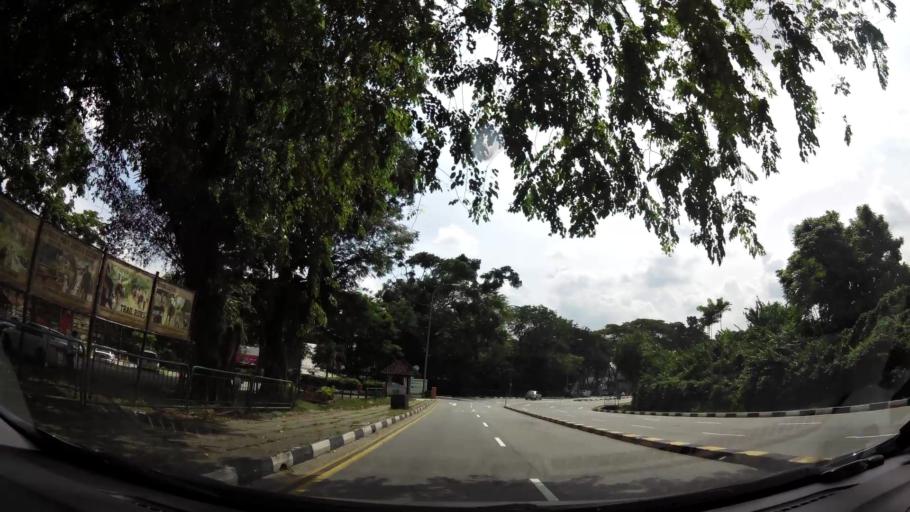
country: SG
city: Singapore
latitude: 1.3337
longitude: 103.7952
